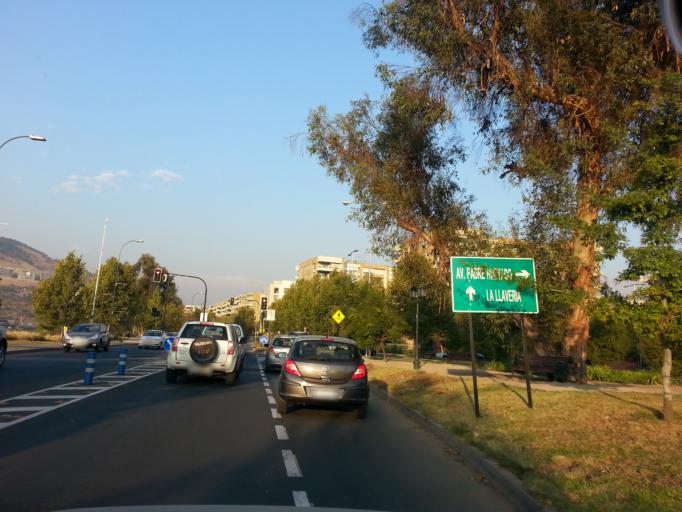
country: CL
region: Santiago Metropolitan
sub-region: Provincia de Santiago
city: Villa Presidente Frei, Nunoa, Santiago, Chile
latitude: -33.3770
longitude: -70.5577
